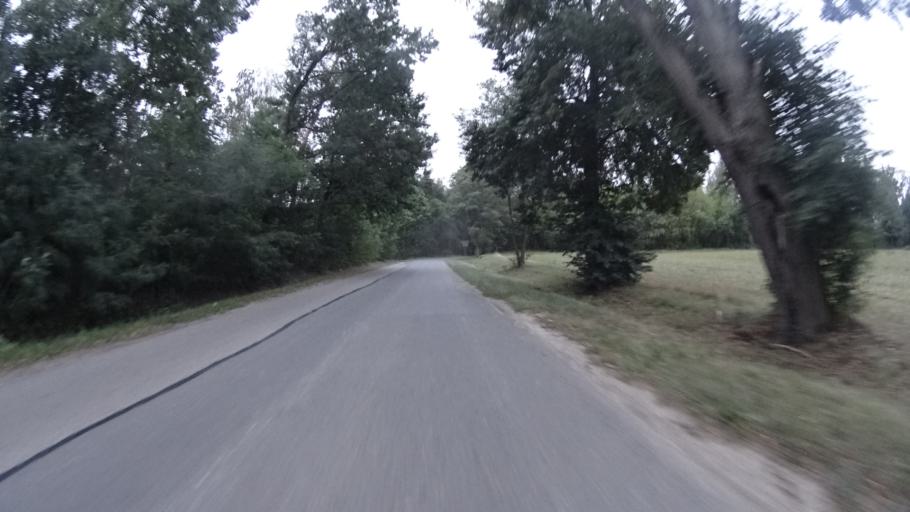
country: PL
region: Masovian Voivodeship
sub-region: Powiat warszawski zachodni
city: Stare Babice
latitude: 52.2741
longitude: 20.8348
